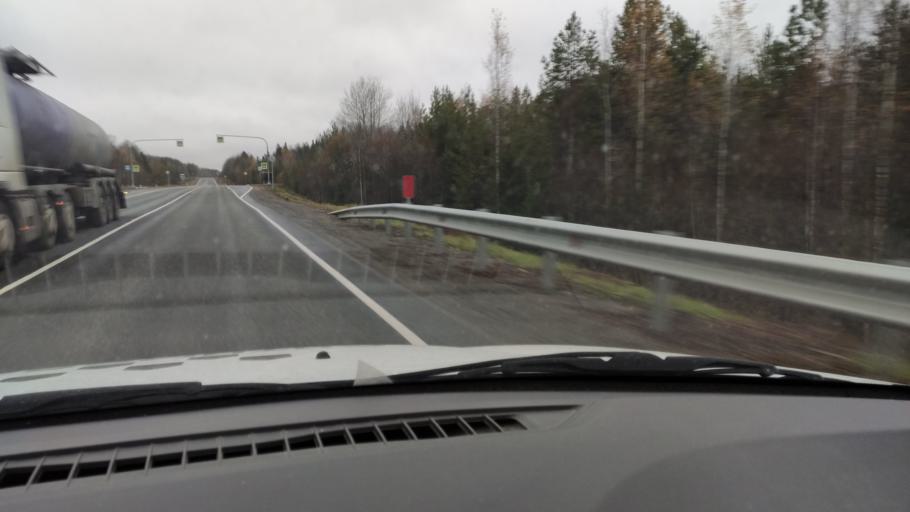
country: RU
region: Kirov
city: Omutninsk
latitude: 58.6966
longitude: 52.1249
